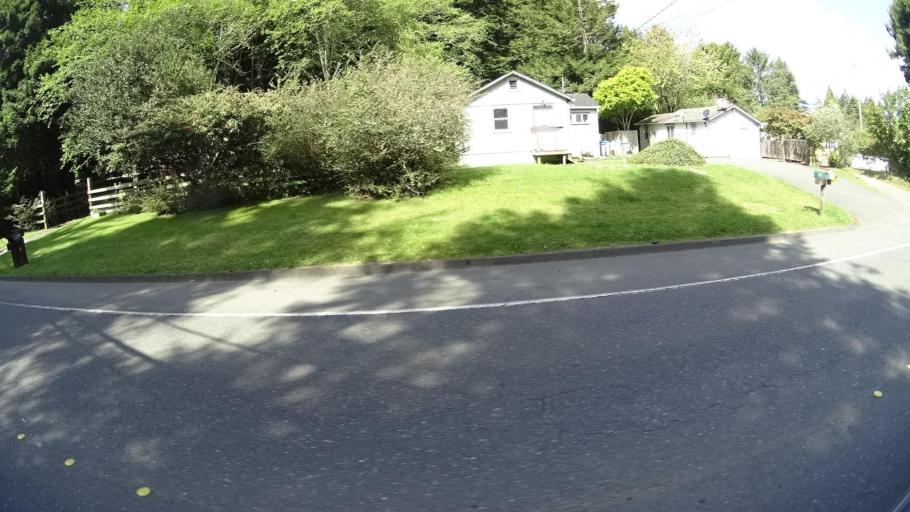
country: US
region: California
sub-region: Humboldt County
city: Cutten
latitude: 40.7518
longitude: -124.1454
